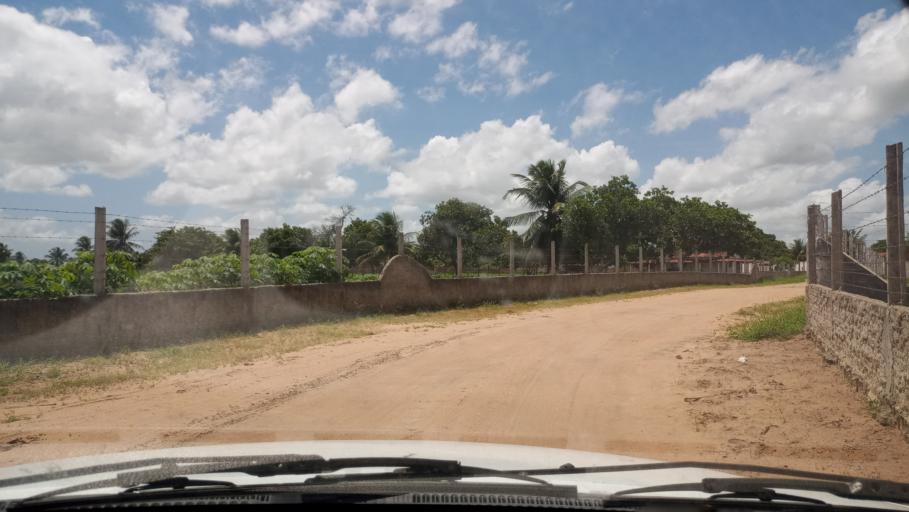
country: BR
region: Rio Grande do Norte
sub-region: Brejinho
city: Brejinho
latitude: -6.2631
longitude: -35.3722
